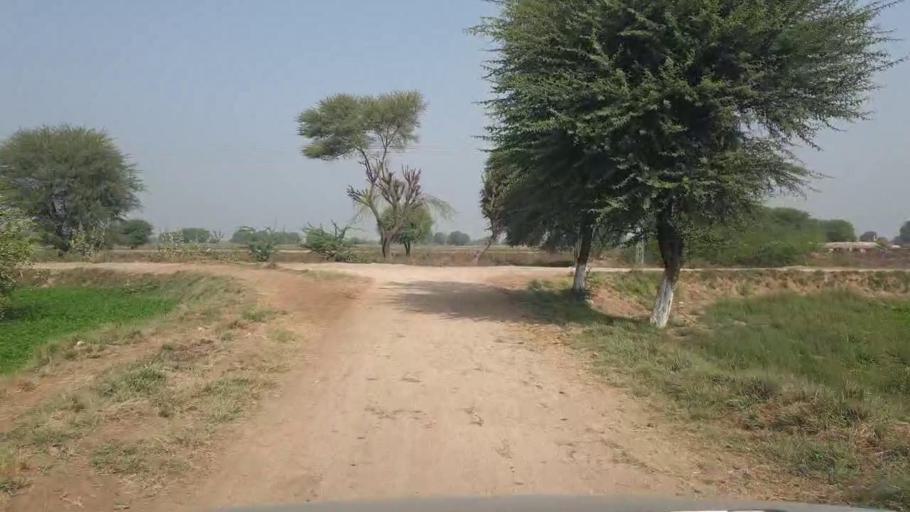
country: PK
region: Sindh
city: Umarkot
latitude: 25.3942
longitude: 69.7093
